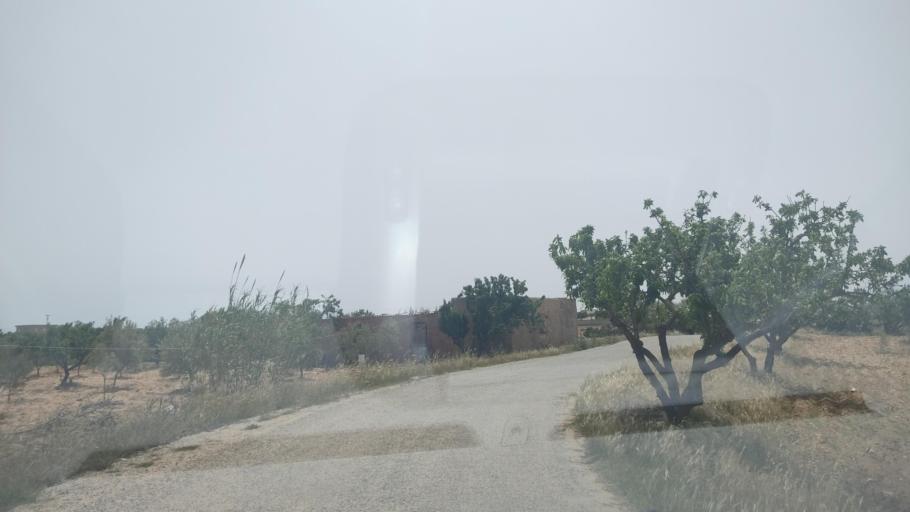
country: TN
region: Safaqis
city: Sfax
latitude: 34.8331
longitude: 10.6007
